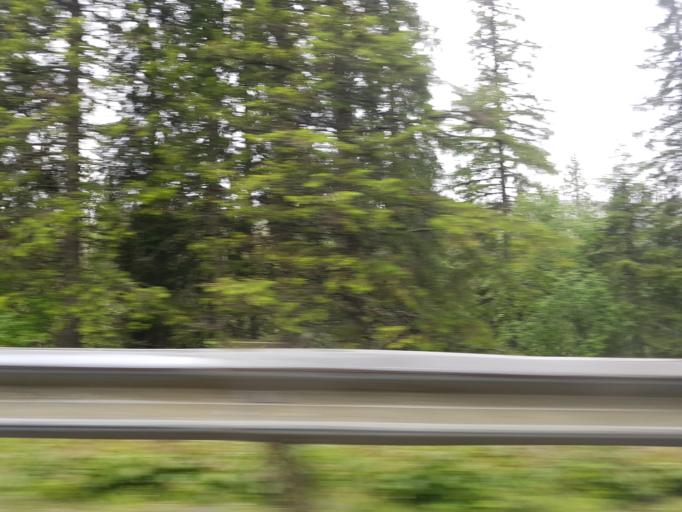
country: NO
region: Sor-Trondelag
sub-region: Selbu
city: Mebonden
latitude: 63.3423
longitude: 11.0774
